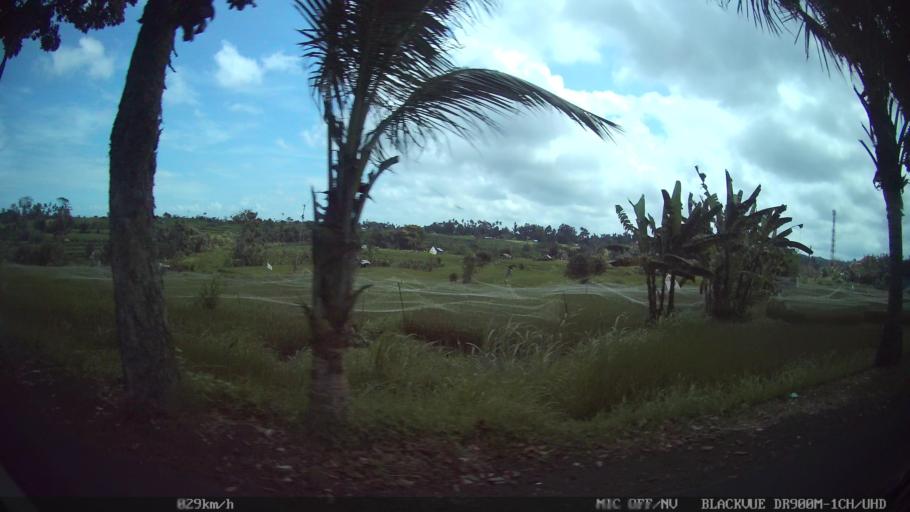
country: ID
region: Bali
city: Klungkung
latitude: -8.5355
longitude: 115.3927
